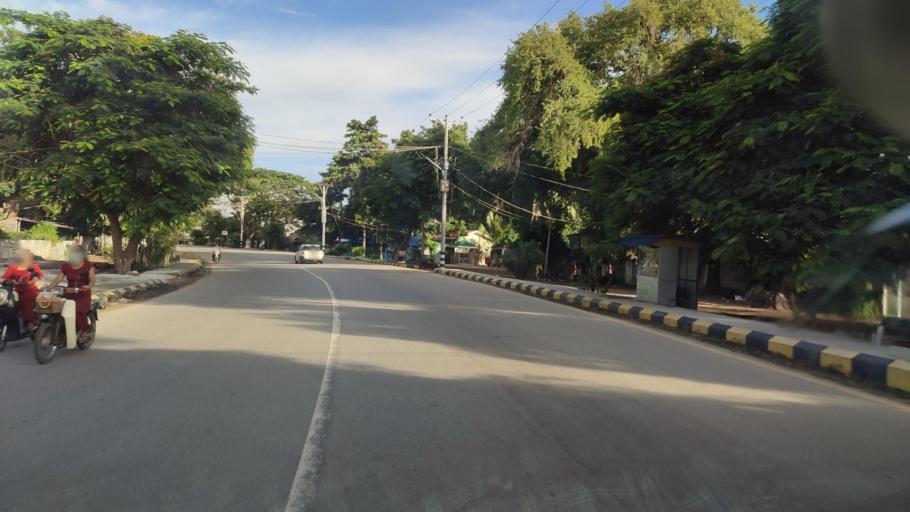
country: MM
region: Mandalay
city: Yamethin
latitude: 20.1360
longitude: 96.1980
